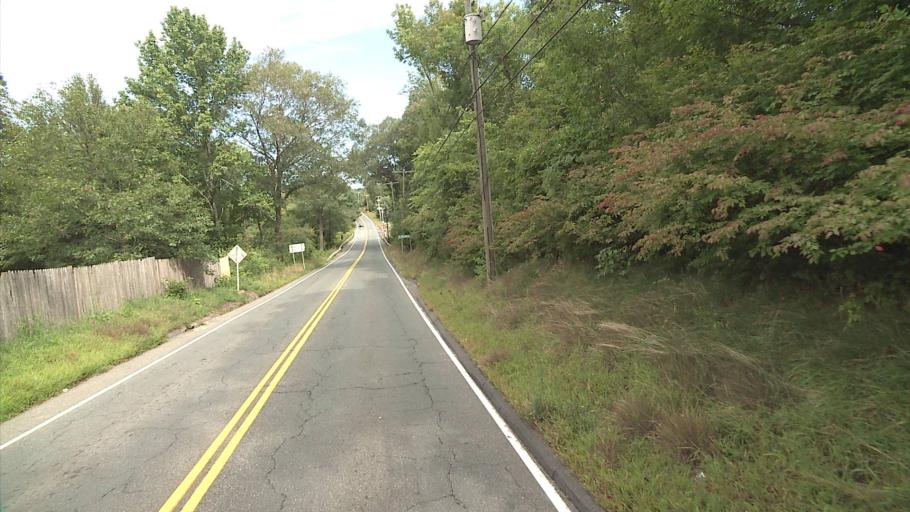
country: US
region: Connecticut
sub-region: Tolland County
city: South Coventry
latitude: 41.7872
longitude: -72.2770
